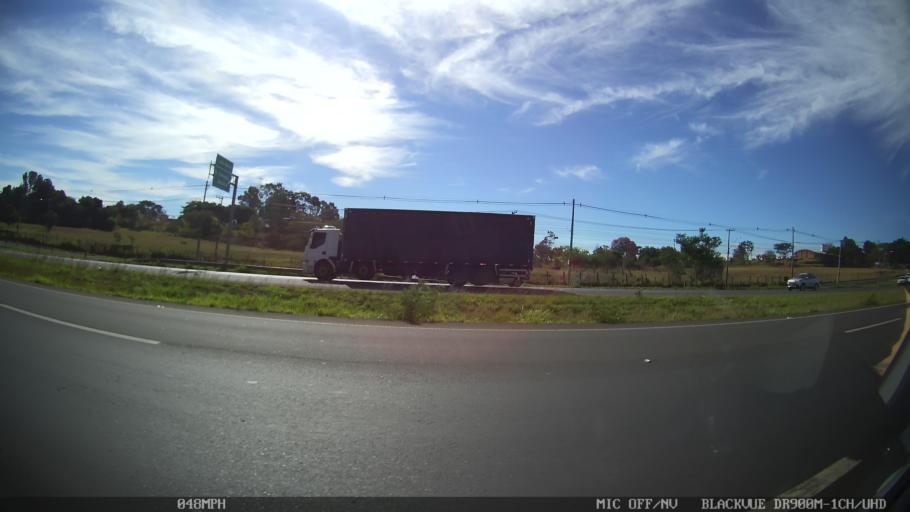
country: BR
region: Sao Paulo
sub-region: Sao Jose Do Rio Preto
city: Sao Jose do Rio Preto
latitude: -20.8021
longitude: -49.3512
